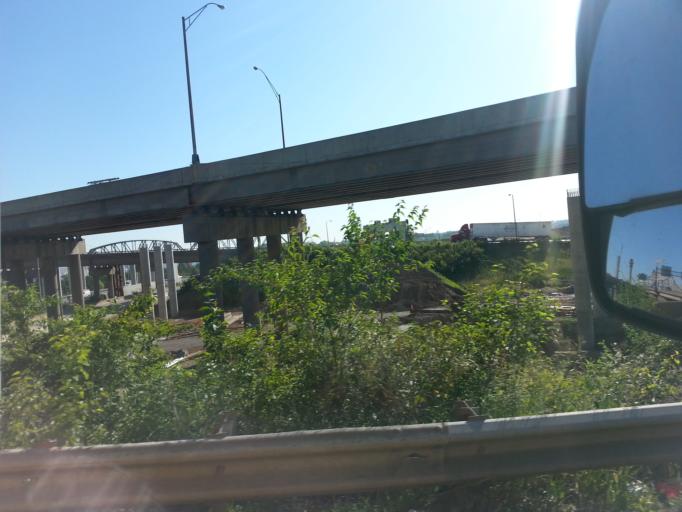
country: US
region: Kentucky
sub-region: Jefferson County
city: Louisville
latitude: 38.2593
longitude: -85.7418
